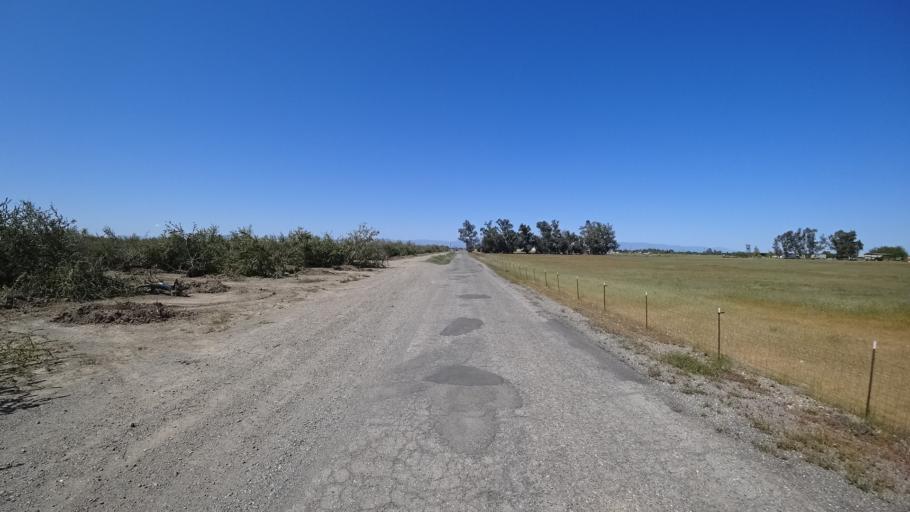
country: US
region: California
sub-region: Glenn County
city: Orland
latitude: 39.7215
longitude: -122.1364
